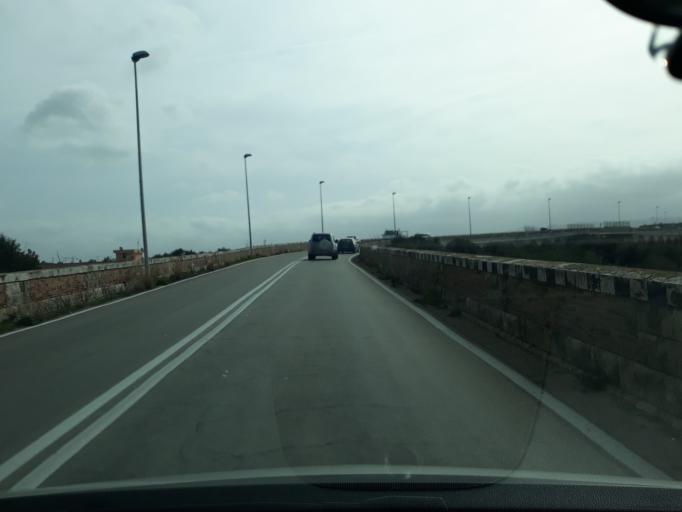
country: IT
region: Apulia
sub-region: Provincia di Bari
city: Monopoli
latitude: 40.9583
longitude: 17.2825
